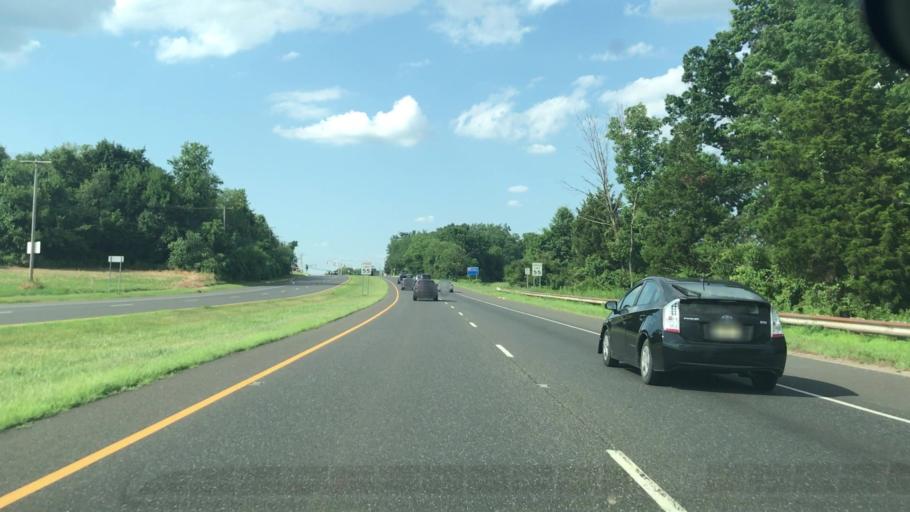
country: US
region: New Jersey
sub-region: Hunterdon County
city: Flemington
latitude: 40.4367
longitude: -74.8590
